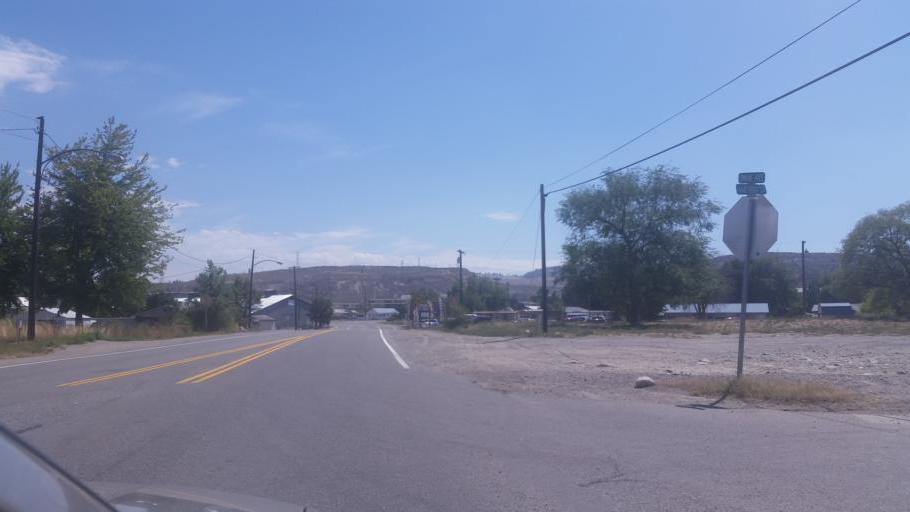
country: US
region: Washington
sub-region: Okanogan County
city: Omak
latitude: 48.4051
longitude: -119.5154
